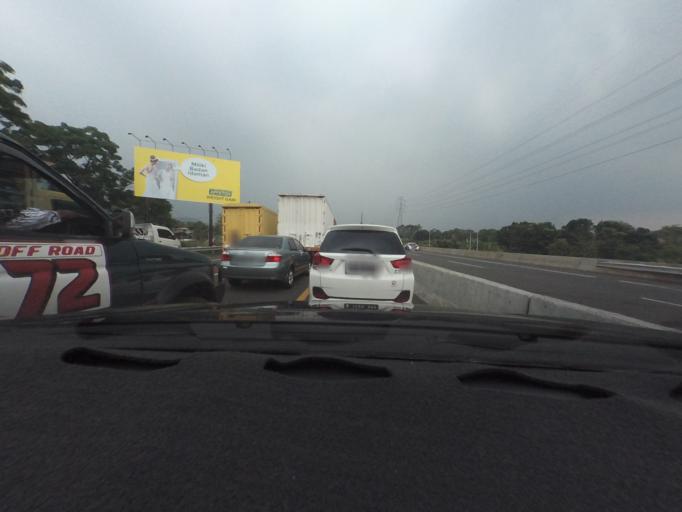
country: ID
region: West Java
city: Bogor
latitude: -6.6341
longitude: 106.8408
